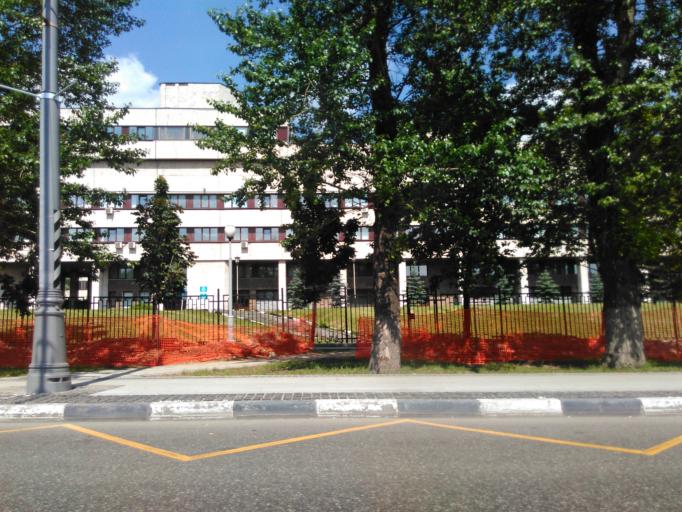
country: RU
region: Moscow
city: Nagornyy
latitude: 55.6569
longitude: 37.6447
